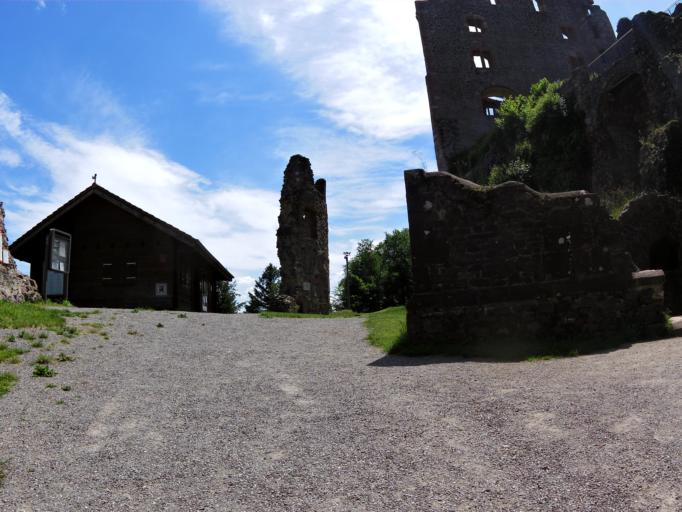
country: DE
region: Baden-Wuerttemberg
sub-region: Freiburg Region
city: Seelbach
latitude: 48.3327
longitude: 7.9802
